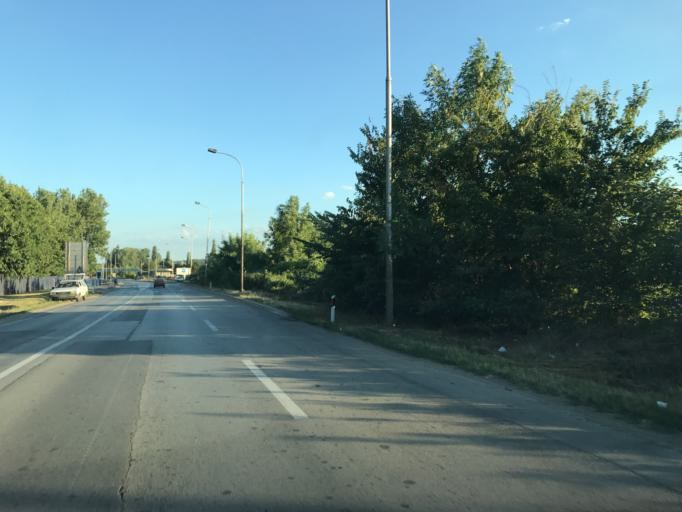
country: RS
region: Central Serbia
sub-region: Podunavski Okrug
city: Smederevo
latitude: 44.6077
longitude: 20.9609
